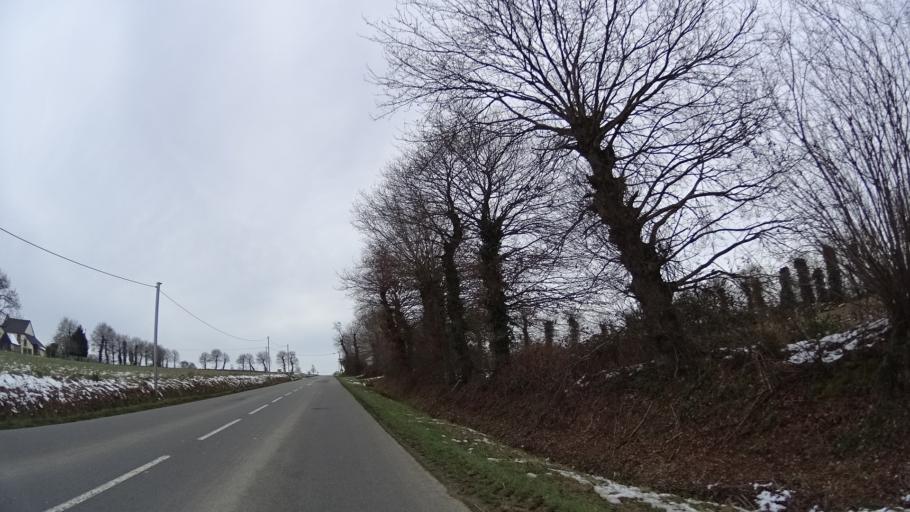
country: FR
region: Brittany
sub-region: Departement d'Ille-et-Vilaine
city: Irodouer
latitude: 48.2685
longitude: -1.9794
